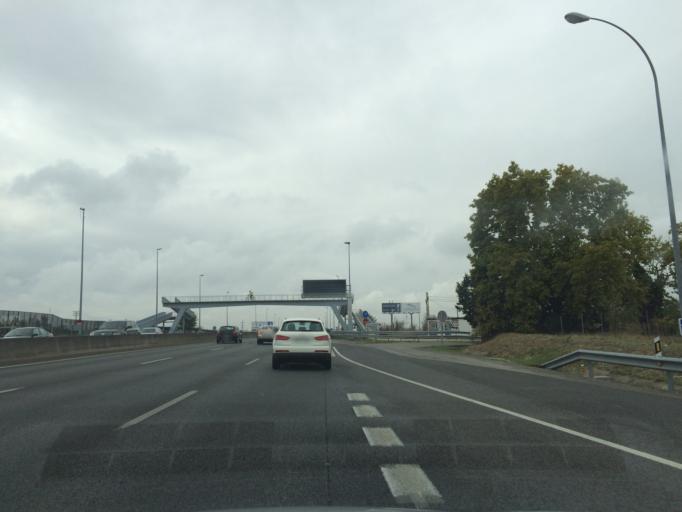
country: ES
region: Madrid
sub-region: Provincia de Madrid
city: Alcorcon
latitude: 40.3692
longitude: -3.8039
